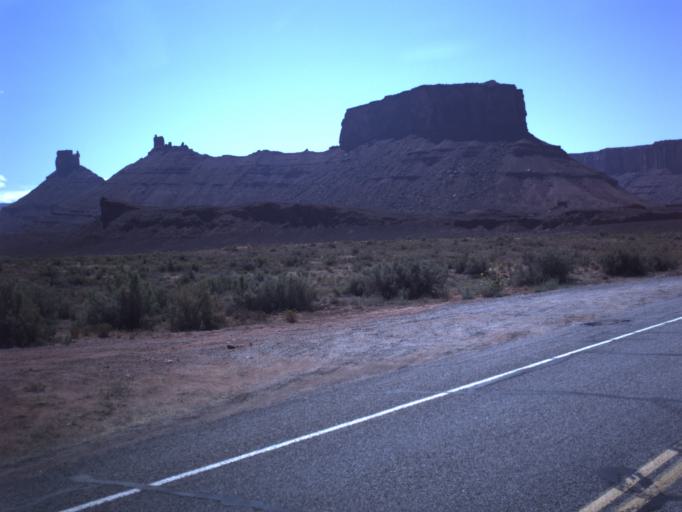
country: US
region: Utah
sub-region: Grand County
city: Moab
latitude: 38.7103
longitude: -109.3768
